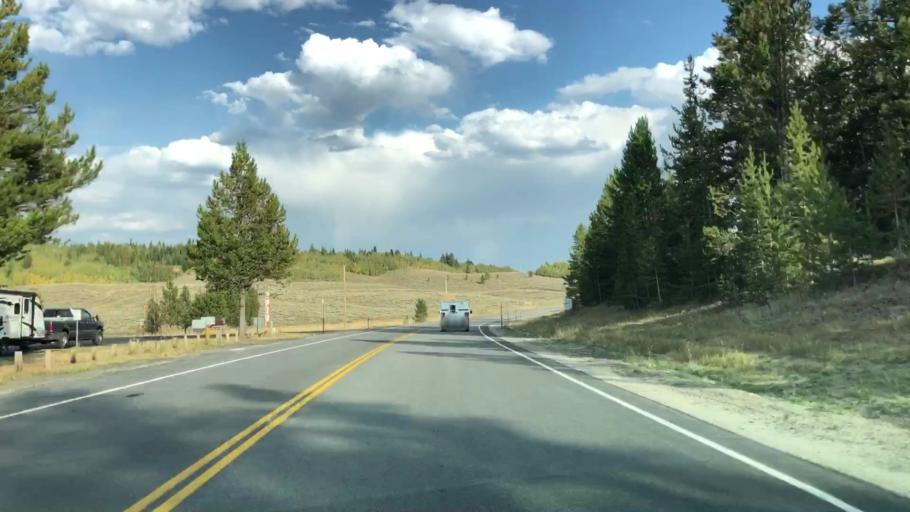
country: US
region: Wyoming
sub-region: Sublette County
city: Pinedale
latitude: 43.1325
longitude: -110.1966
